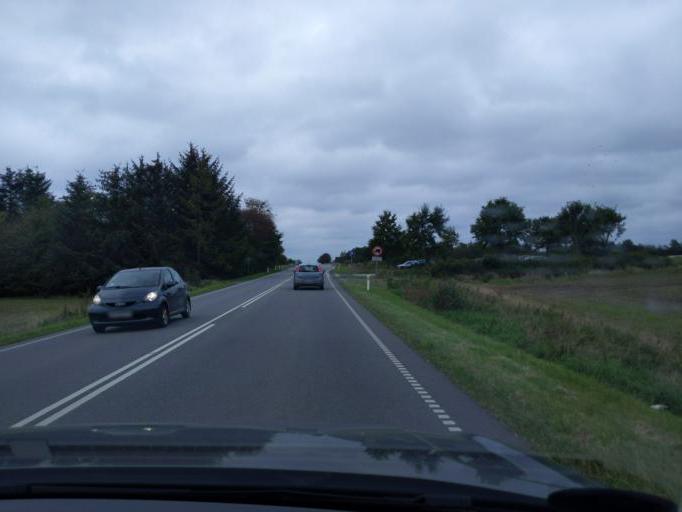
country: DK
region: North Denmark
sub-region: Mariagerfjord Kommune
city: Hobro
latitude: 56.5778
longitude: 9.8135
